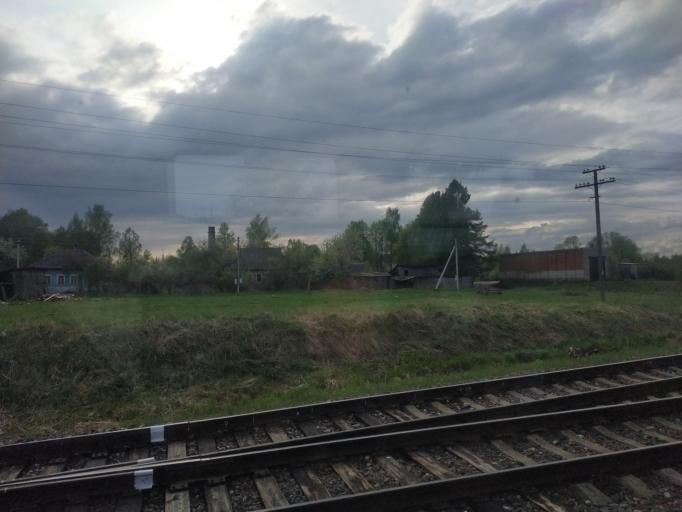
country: RU
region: Smolensk
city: Ugra
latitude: 54.7727
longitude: 34.3428
